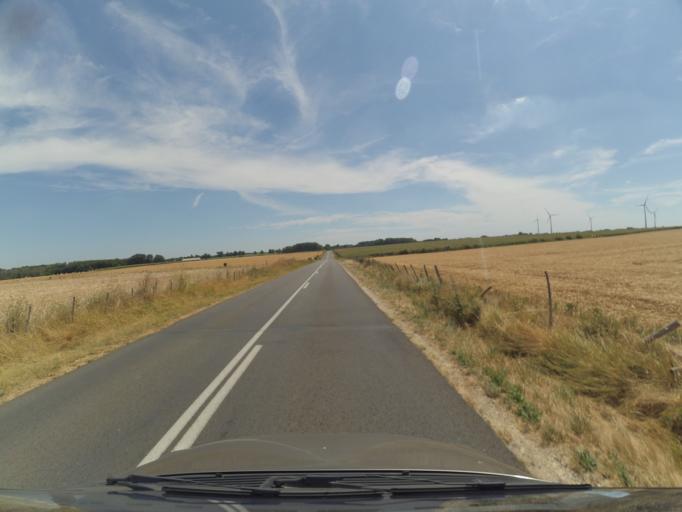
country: FR
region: Poitou-Charentes
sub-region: Departement de la Vienne
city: Saint-Maurice-la-Clouere
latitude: 46.3415
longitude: 0.4590
